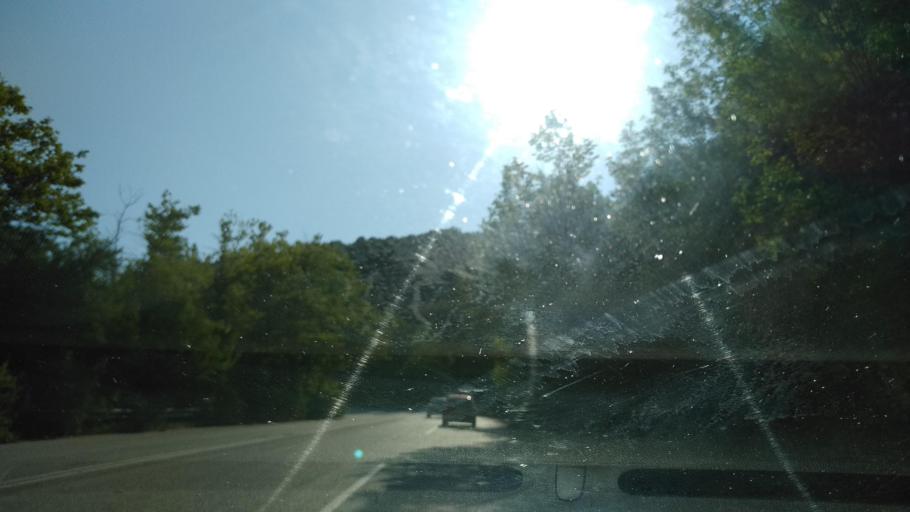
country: GR
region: Central Macedonia
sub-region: Nomos Chalkidikis
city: Stratonion
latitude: 40.5472
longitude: 23.8235
